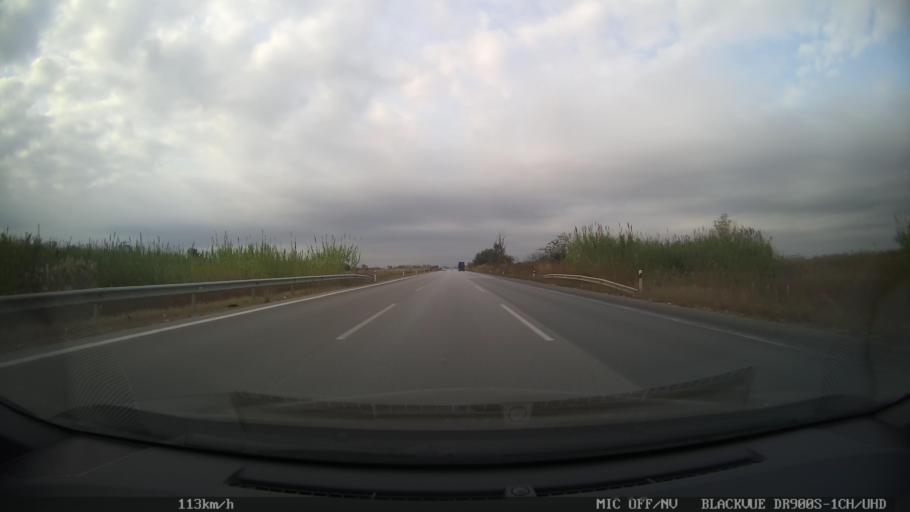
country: GR
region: Central Macedonia
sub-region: Nomos Thessalonikis
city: Chalastra
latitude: 40.6295
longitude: 22.7728
